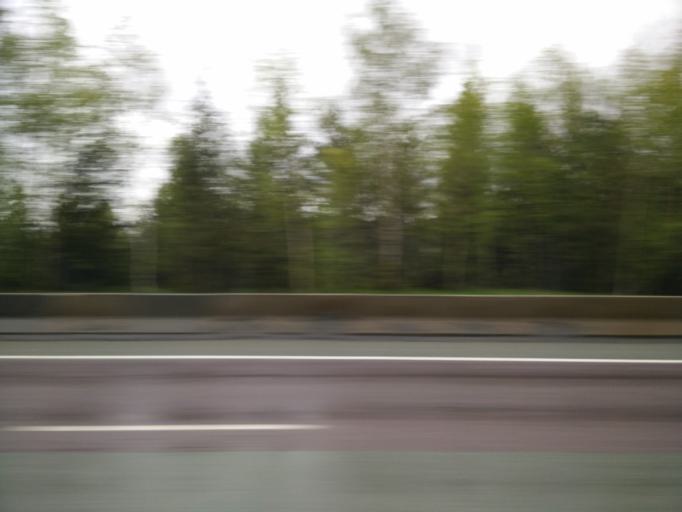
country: NO
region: Sor-Trondelag
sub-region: Malvik
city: Hommelvik
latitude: 63.4150
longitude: 10.7685
